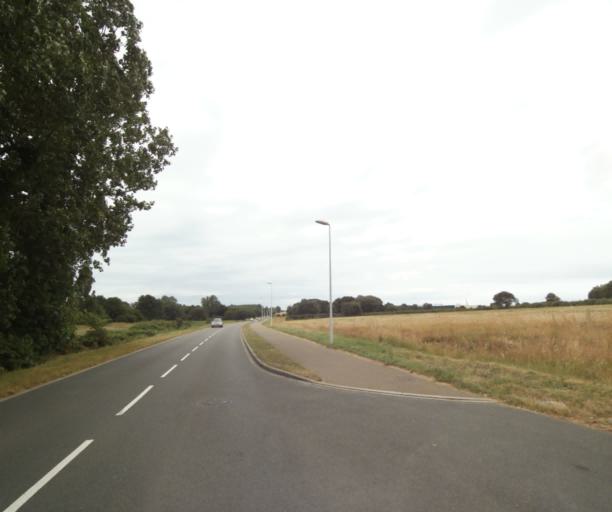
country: FR
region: Pays de la Loire
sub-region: Departement de la Vendee
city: Chateau-d'Olonne
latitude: 46.4957
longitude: -1.7427
